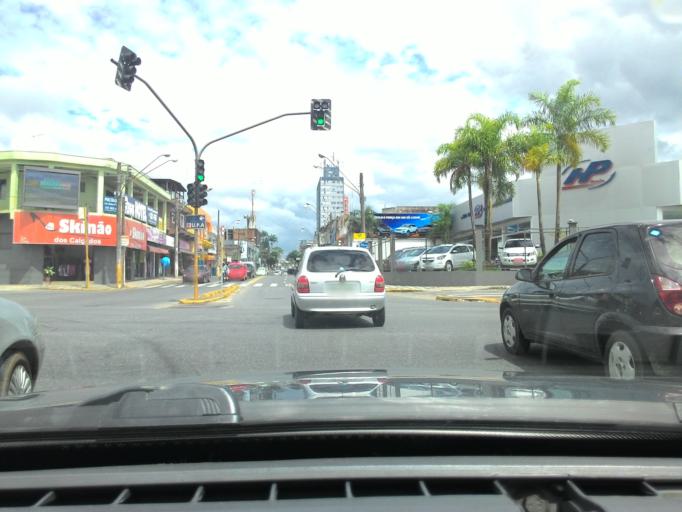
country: BR
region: Sao Paulo
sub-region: Registro
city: Registro
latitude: -24.4971
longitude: -47.8417
